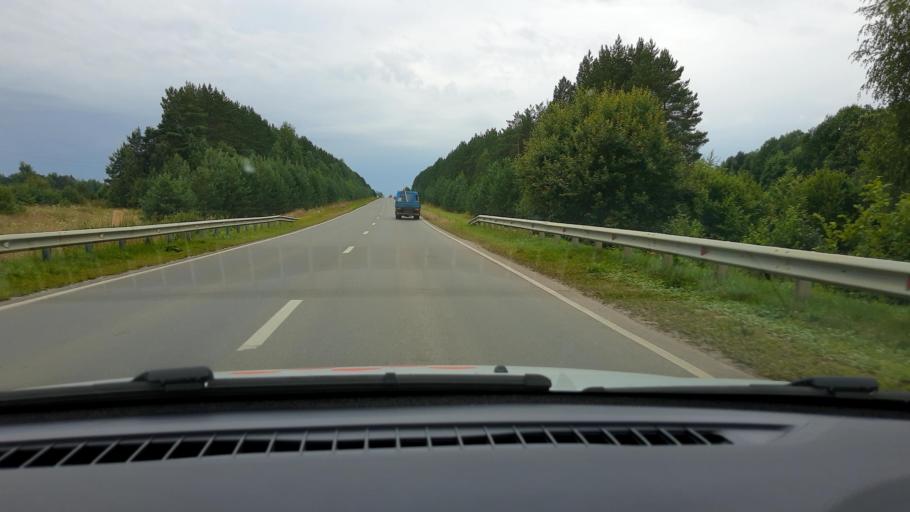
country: RU
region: Nizjnij Novgorod
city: Vyyezdnoye
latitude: 55.1610
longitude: 43.5826
